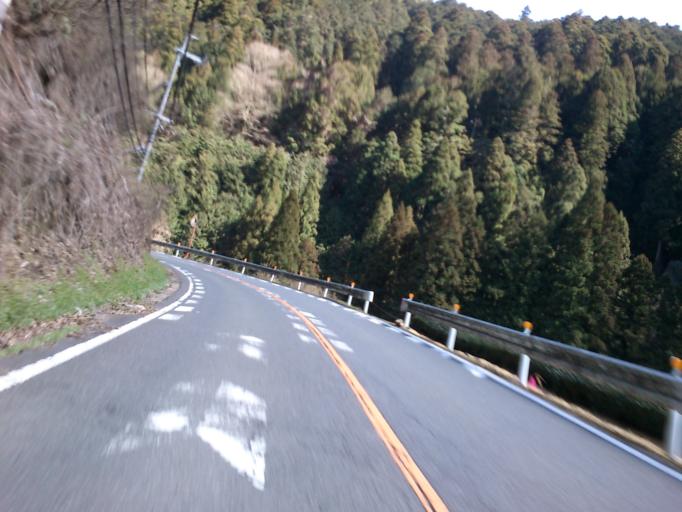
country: JP
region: Kyoto
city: Uji
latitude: 34.8133
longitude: 135.9245
